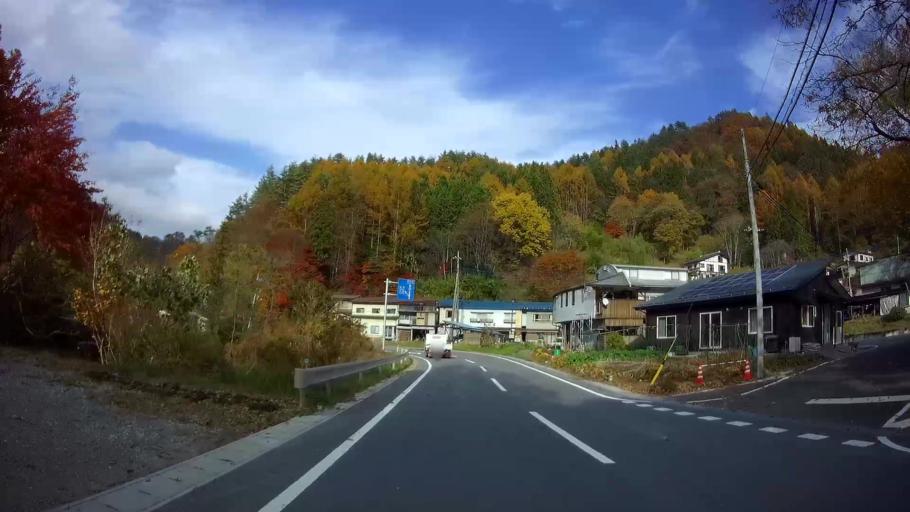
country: JP
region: Gunma
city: Nakanojomachi
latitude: 36.6442
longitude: 138.6492
